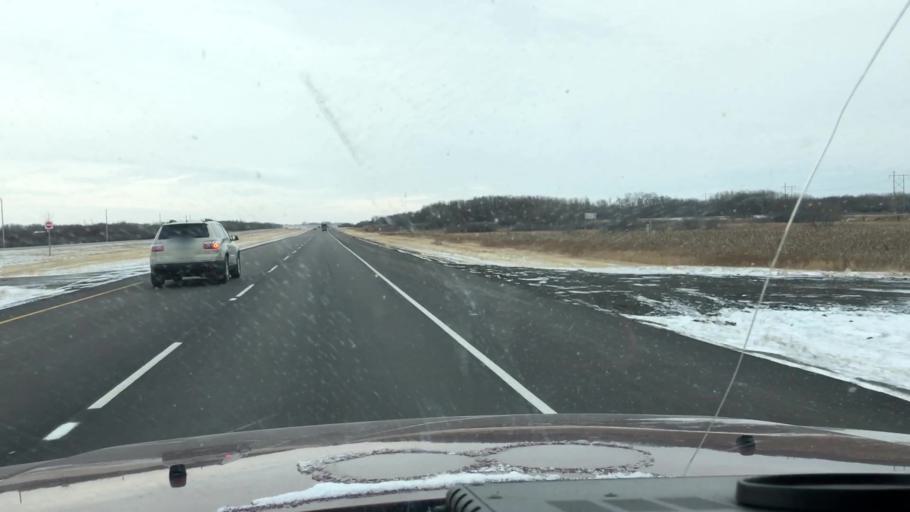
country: CA
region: Saskatchewan
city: Saskatoon
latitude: 51.8821
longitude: -106.5131
